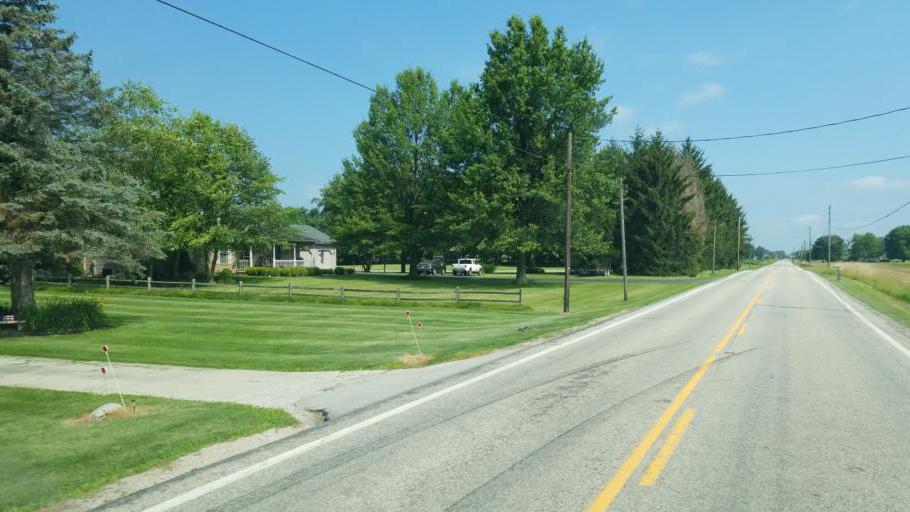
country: US
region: Ohio
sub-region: Crawford County
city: Galion
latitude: 40.7710
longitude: -82.8574
